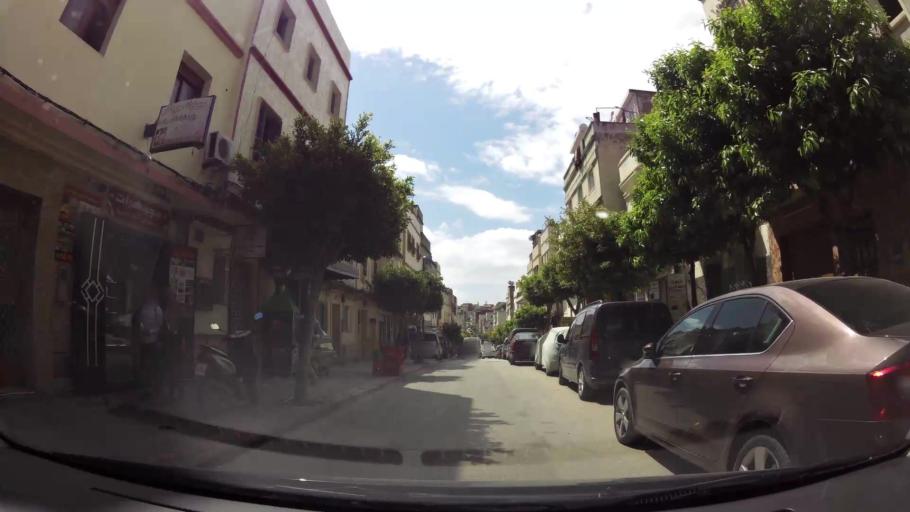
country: MA
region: Tanger-Tetouan
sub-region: Tanger-Assilah
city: Tangier
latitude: 35.7678
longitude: -5.8269
